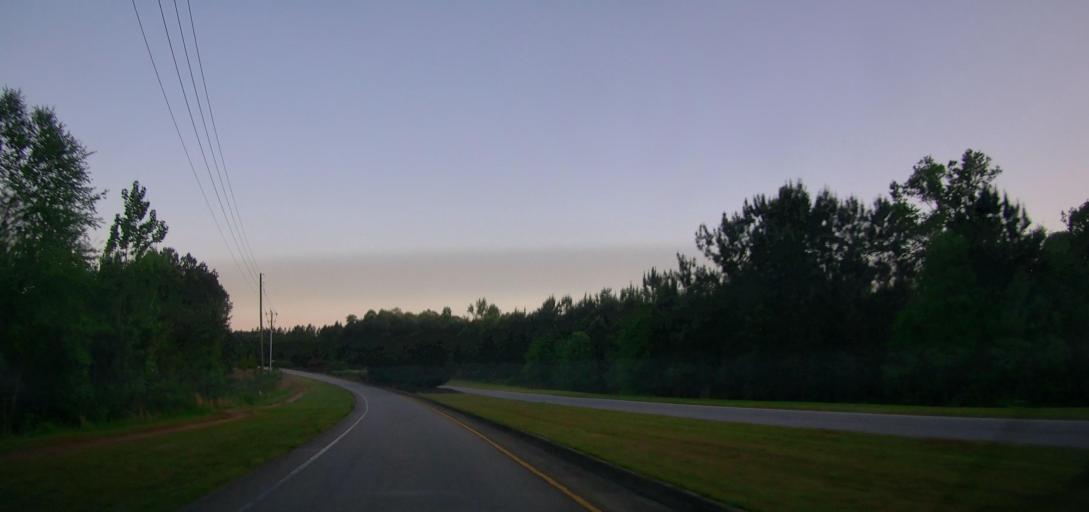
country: US
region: Georgia
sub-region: Henry County
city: McDonough
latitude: 33.4536
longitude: -84.1948
